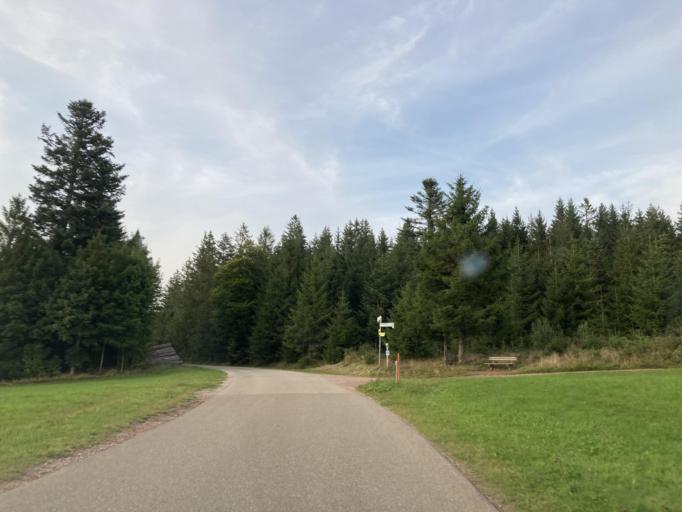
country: DE
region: Baden-Wuerttemberg
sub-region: Freiburg Region
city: Schonwald im Schwarzwald
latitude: 48.1026
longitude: 8.1728
